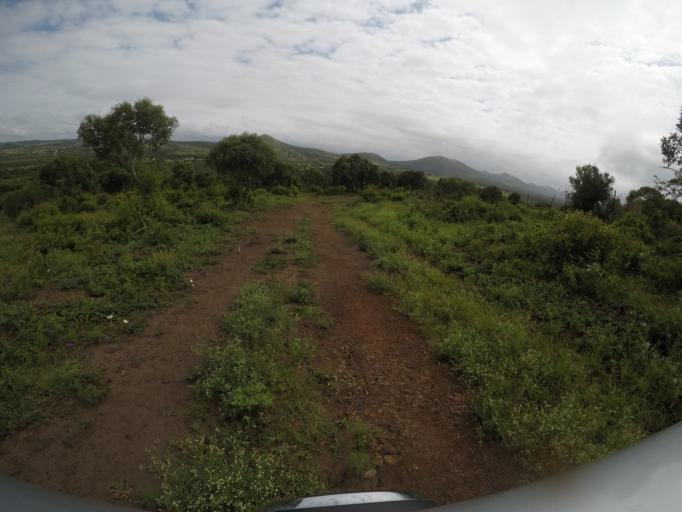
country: ZA
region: KwaZulu-Natal
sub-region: uThungulu District Municipality
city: Empangeni
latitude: -28.6260
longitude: 31.8630
